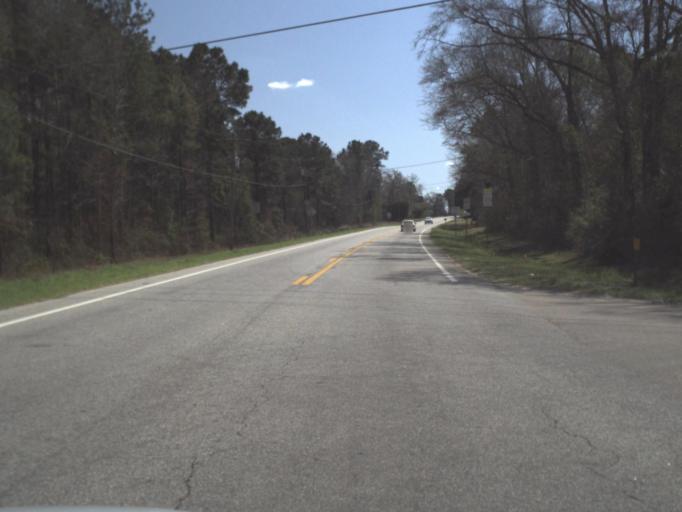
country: US
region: Florida
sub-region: Gadsden County
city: Gretna
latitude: 30.6609
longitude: -84.6069
